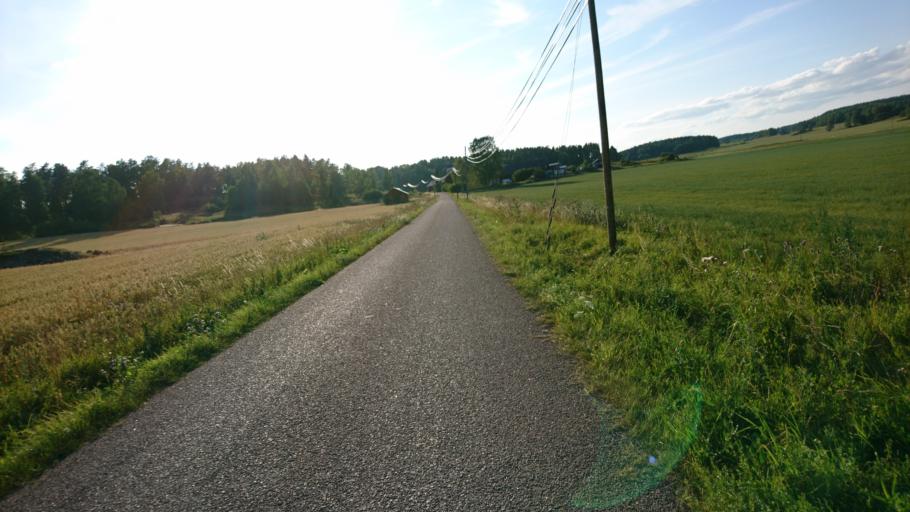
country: SE
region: Soedermanland
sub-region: Strangnas Kommun
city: Stallarholmen
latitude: 59.4022
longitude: 17.2885
